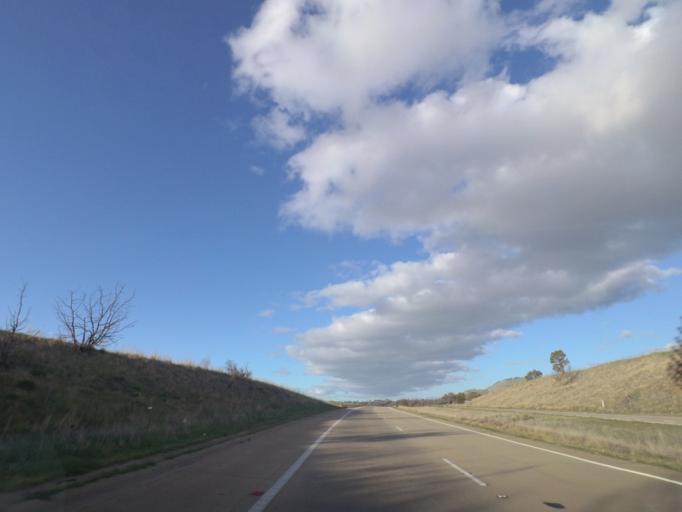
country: AU
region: New South Wales
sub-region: Gundagai
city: Gundagai
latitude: -34.8109
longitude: 148.4528
